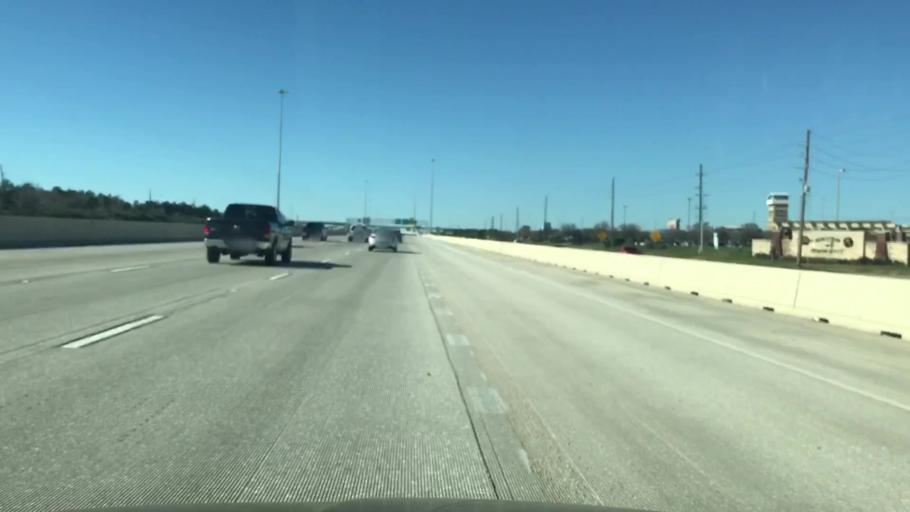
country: US
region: Texas
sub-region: Harris County
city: Cypress
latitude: 29.9934
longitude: -95.7531
